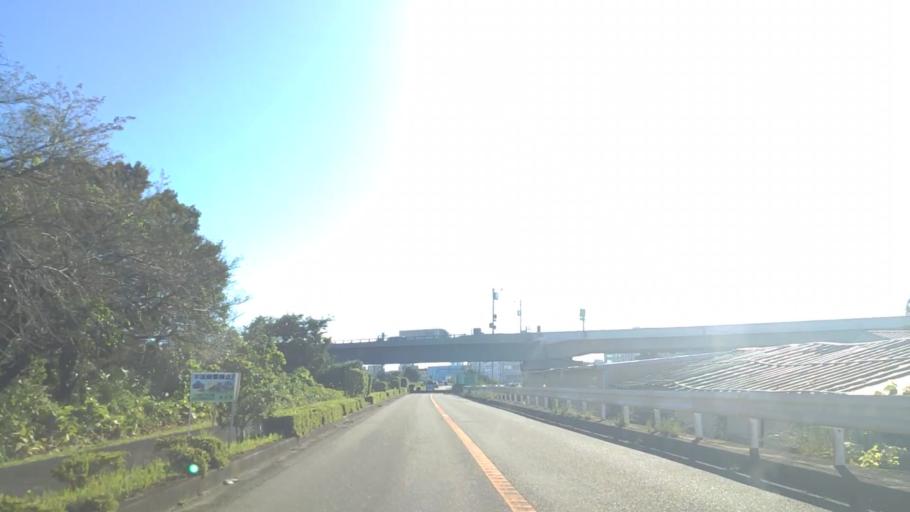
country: JP
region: Kanagawa
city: Atsugi
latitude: 35.4573
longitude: 139.3736
